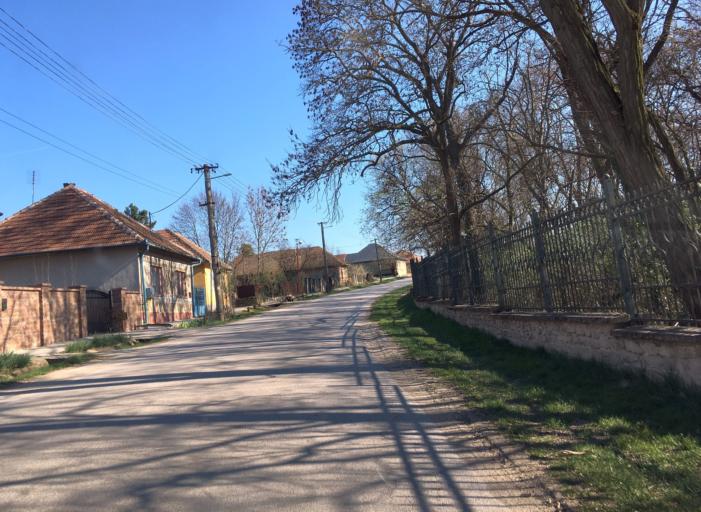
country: HU
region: Komarom-Esztergom
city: Nyergesujfalu
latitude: 47.8297
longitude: 18.5994
